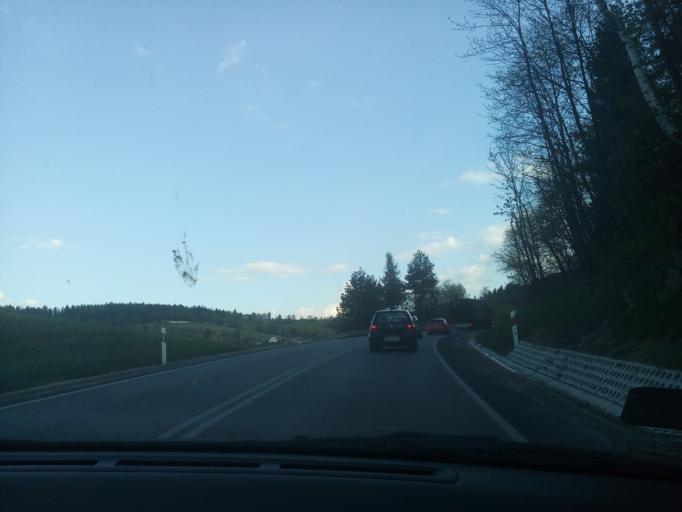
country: PL
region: Lesser Poland Voivodeship
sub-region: Powiat nowosadecki
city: Krynica-Zdroj
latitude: 49.4732
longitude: 20.9453
